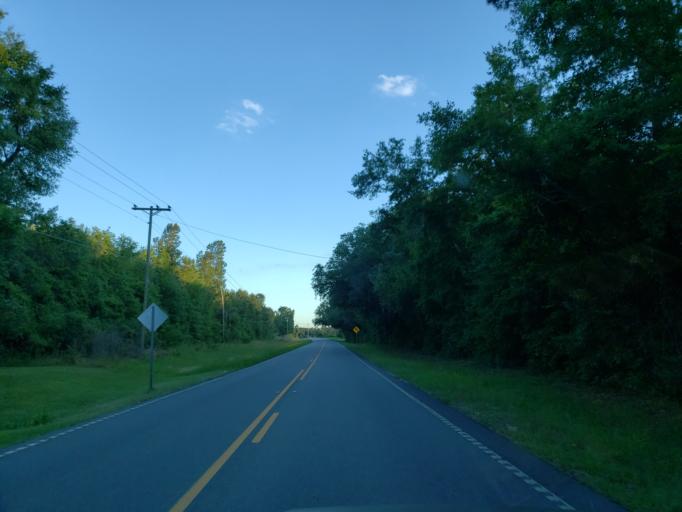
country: US
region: Georgia
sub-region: Lowndes County
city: Valdosta
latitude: 30.7288
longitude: -83.2483
